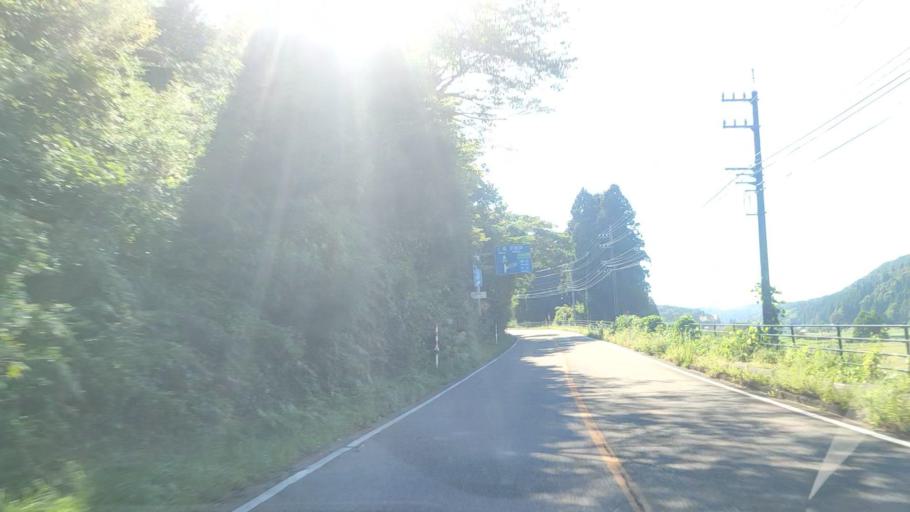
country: JP
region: Ishikawa
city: Nanao
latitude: 37.3496
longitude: 137.2333
